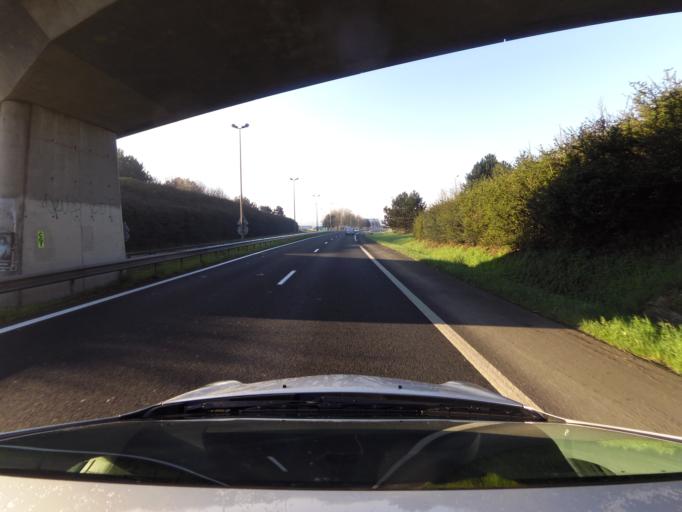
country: FR
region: Lower Normandy
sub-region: Departement du Calvados
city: Authie
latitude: 49.1901
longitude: -0.4240
